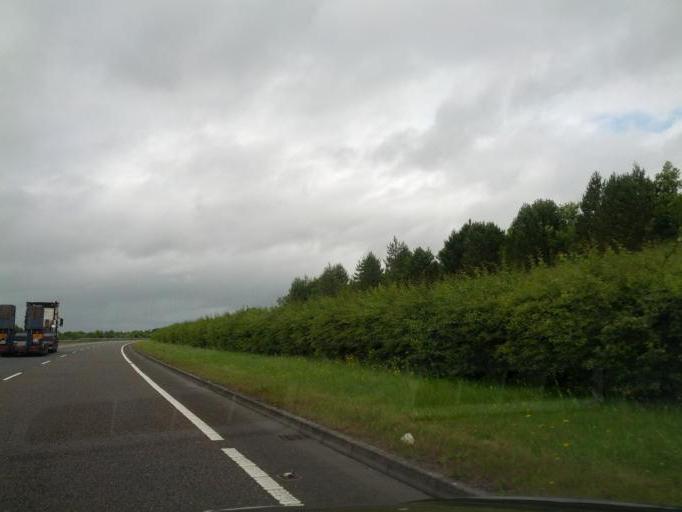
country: IE
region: Munster
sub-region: An Clar
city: Newmarket on Fergus
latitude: 52.7761
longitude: -8.9200
